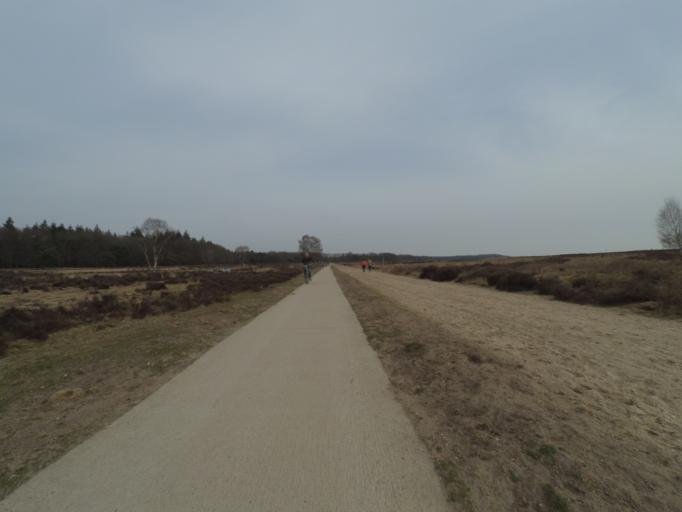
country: NL
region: Gelderland
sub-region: Gemeente Ede
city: Ede
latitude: 52.0494
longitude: 5.7059
